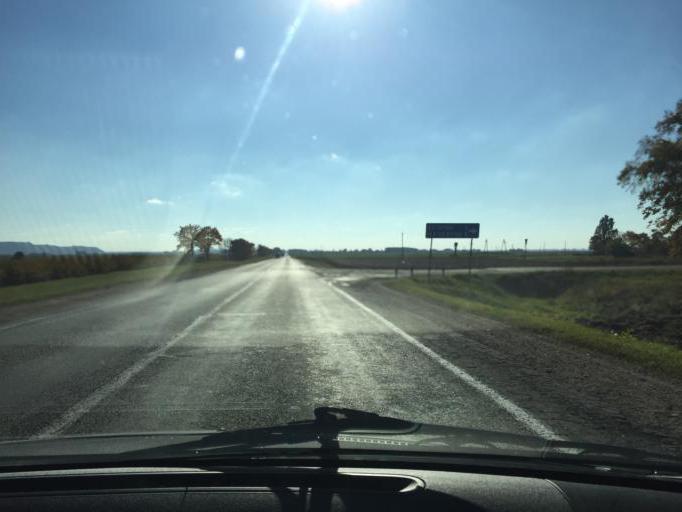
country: BY
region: Minsk
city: Slutsk
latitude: 52.9366
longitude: 27.4891
